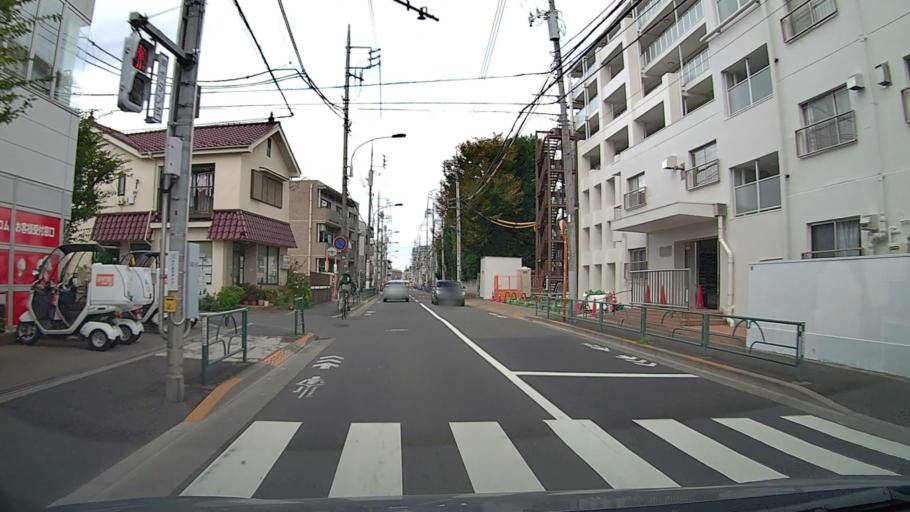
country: JP
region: Saitama
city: Wako
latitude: 35.7463
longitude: 139.6107
